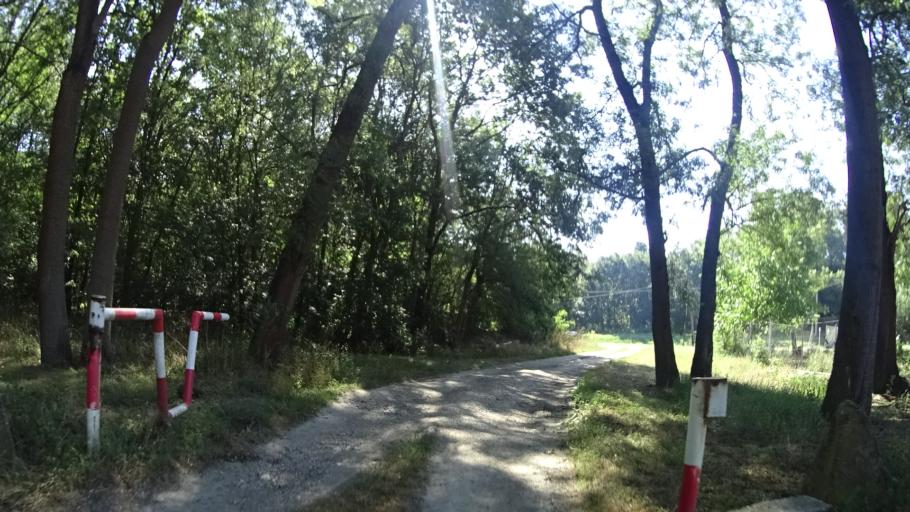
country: CZ
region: South Moravian
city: Hodonin
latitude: 48.8142
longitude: 17.1087
